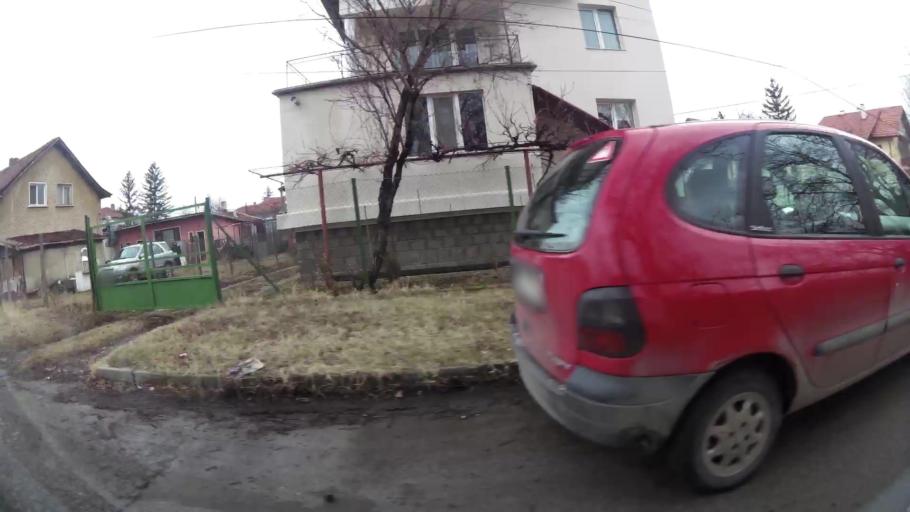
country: BG
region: Sofiya
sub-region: Obshtina Bozhurishte
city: Bozhurishte
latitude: 42.7409
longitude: 23.2656
